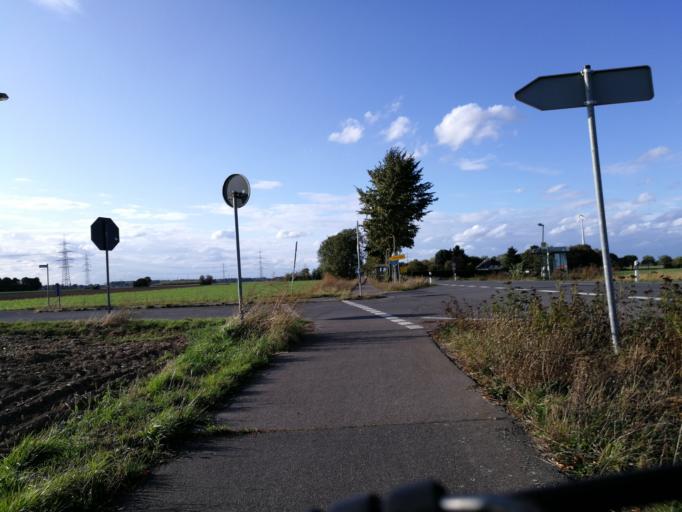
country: DE
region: North Rhine-Westphalia
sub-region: Regierungsbezirk Dusseldorf
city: Neubrueck
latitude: 51.1203
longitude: 6.7060
